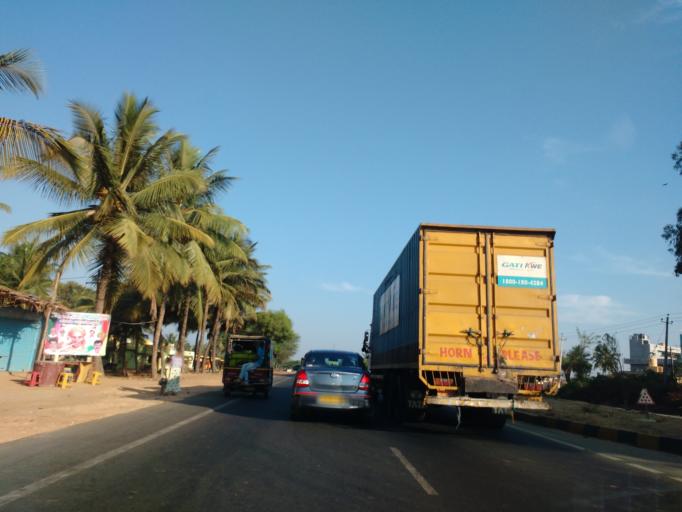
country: IN
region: Karnataka
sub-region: Bangalore Rural
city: Nelamangala
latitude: 13.1698
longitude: 77.3094
